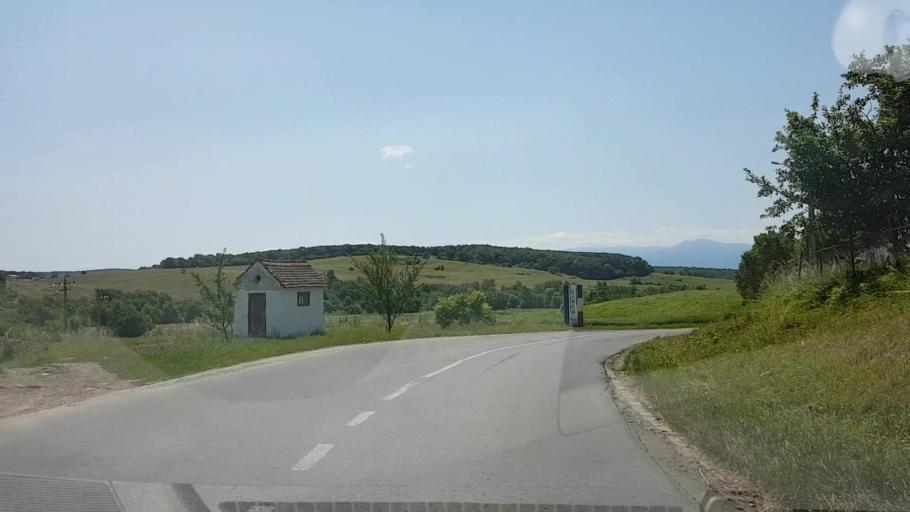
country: RO
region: Brasov
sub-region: Comuna Cincu
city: Cincu
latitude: 45.9075
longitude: 24.8113
